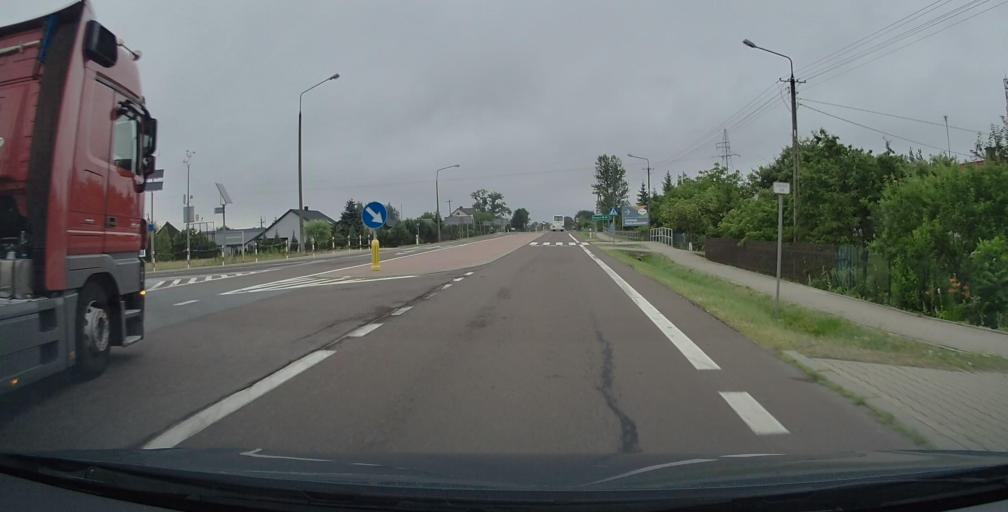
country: PL
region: Lublin Voivodeship
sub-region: Powiat bialski
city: Zalesie
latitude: 52.0371
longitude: 23.4709
